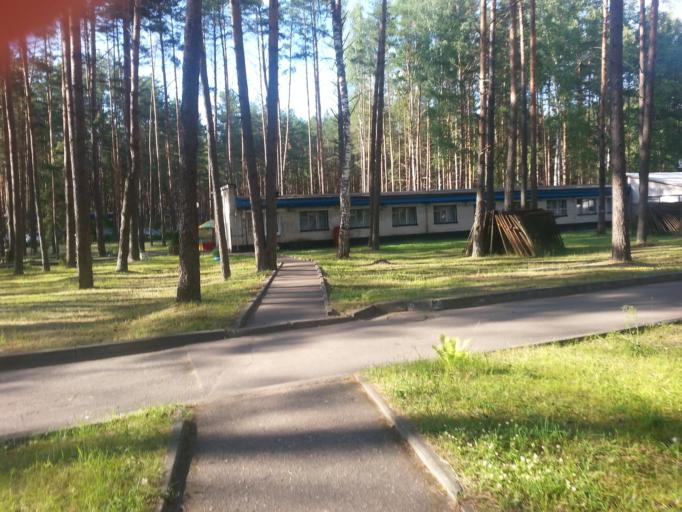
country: BY
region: Grodnenskaya
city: Skidal'
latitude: 53.8027
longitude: 24.1835
